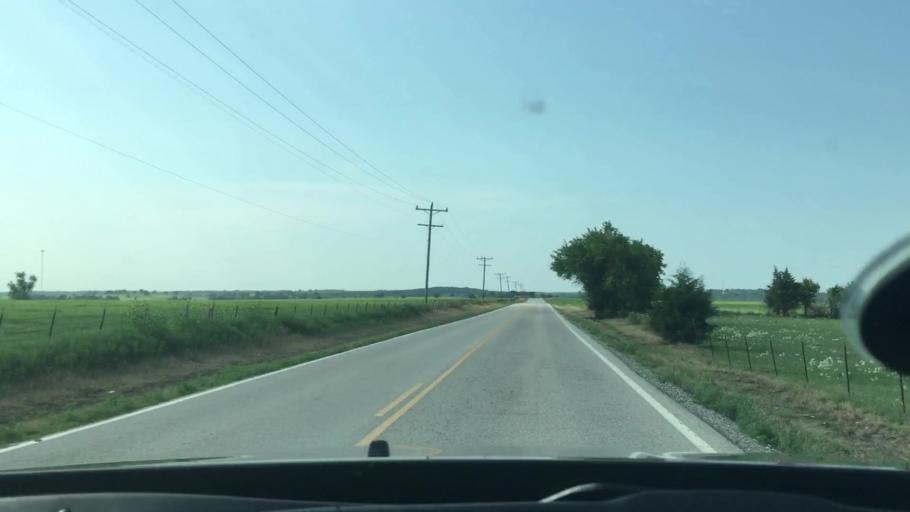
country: US
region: Oklahoma
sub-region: Bryan County
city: Durant
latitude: 34.1099
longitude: -96.4877
